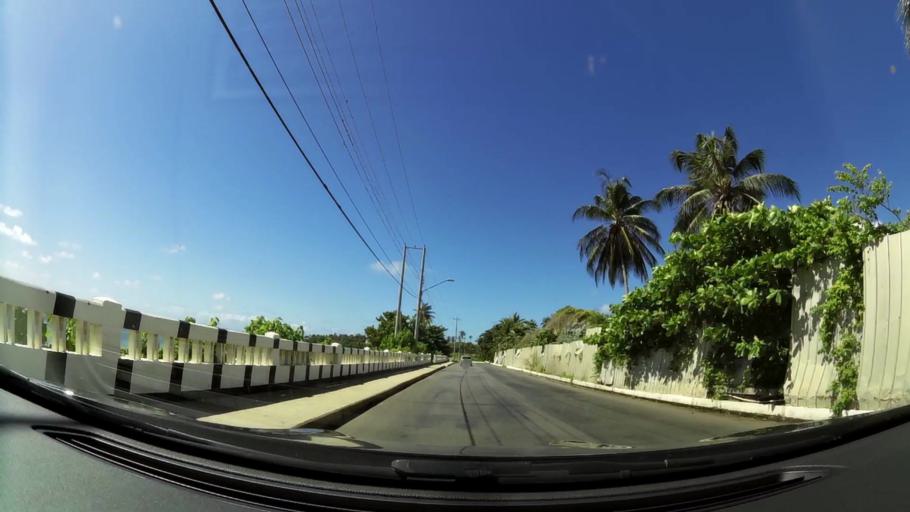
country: TT
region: Tobago
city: Scarborough
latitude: 11.1657
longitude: -60.7634
